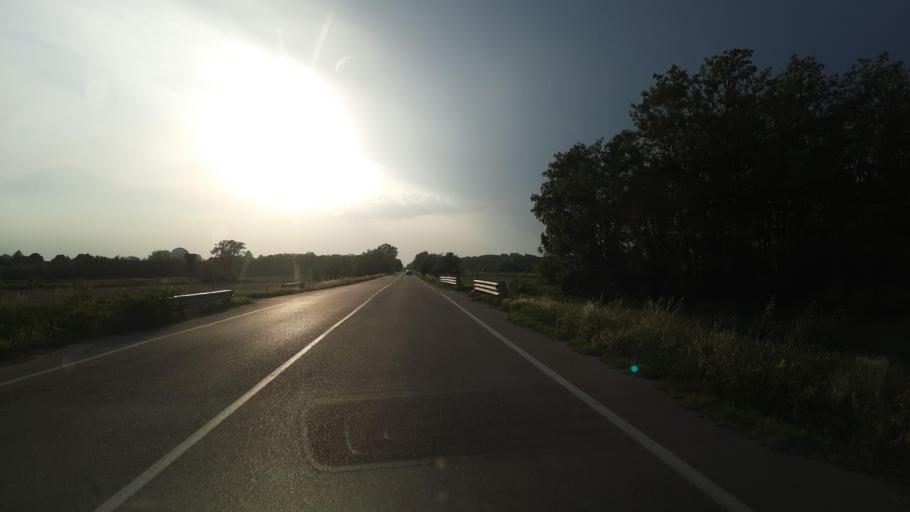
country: IT
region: Lombardy
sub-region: Provincia di Pavia
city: Cergnago
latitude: 45.2306
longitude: 8.8130
